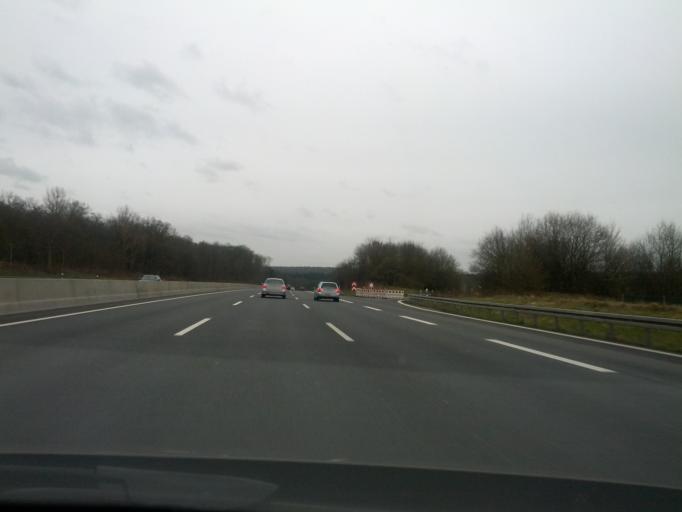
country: DE
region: Lower Saxony
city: Haverlah
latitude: 52.0607
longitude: 10.1929
